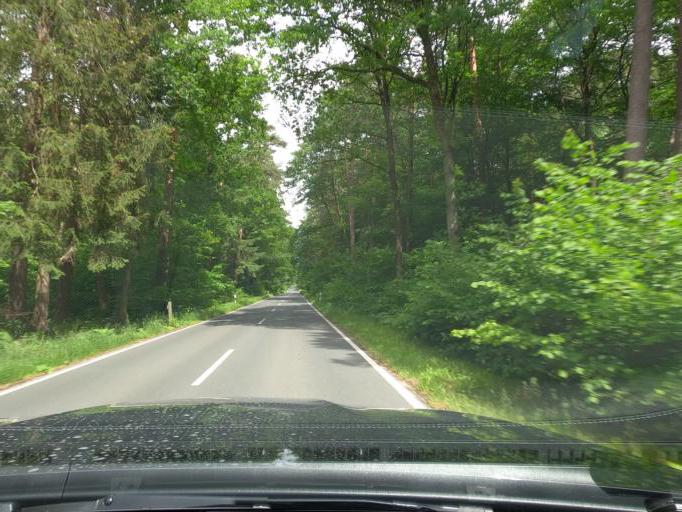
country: DE
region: Lower Saxony
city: Lehrte
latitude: 52.3983
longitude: 9.9264
